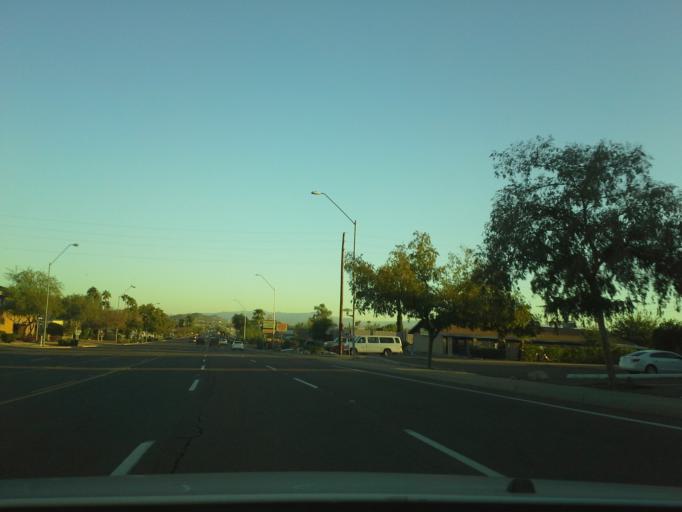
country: US
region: Arizona
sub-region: Maricopa County
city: Paradise Valley
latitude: 33.6197
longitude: -112.0306
